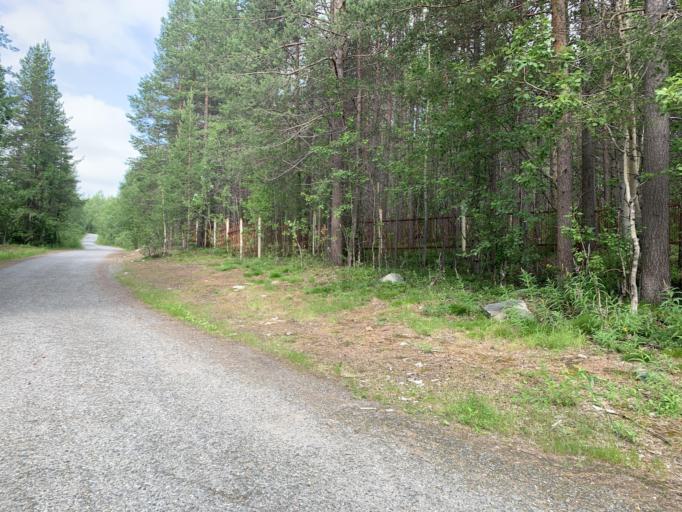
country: RU
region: Murmansk
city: Afrikanda
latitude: 67.6527
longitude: 32.8907
